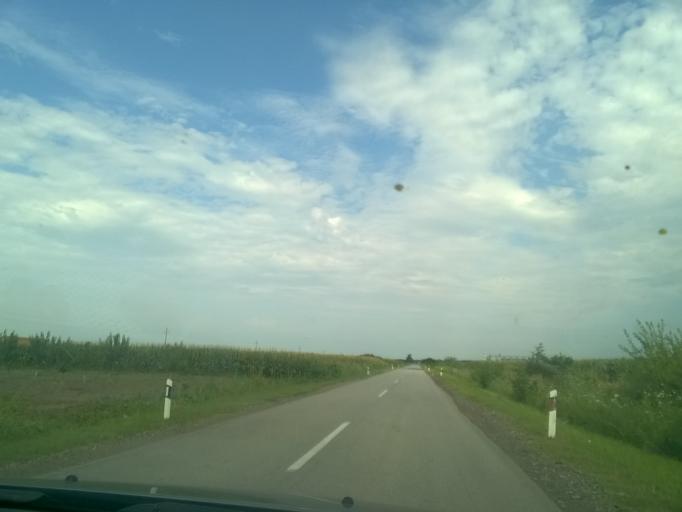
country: RS
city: Stajicevo
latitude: 45.3145
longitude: 20.4694
